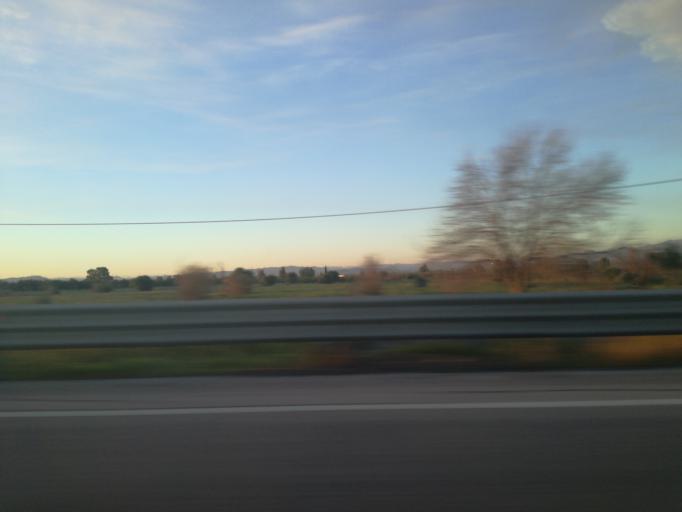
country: IT
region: Sicily
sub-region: Catania
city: Motta Sant'Anastasia
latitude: 37.4276
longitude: 14.9288
